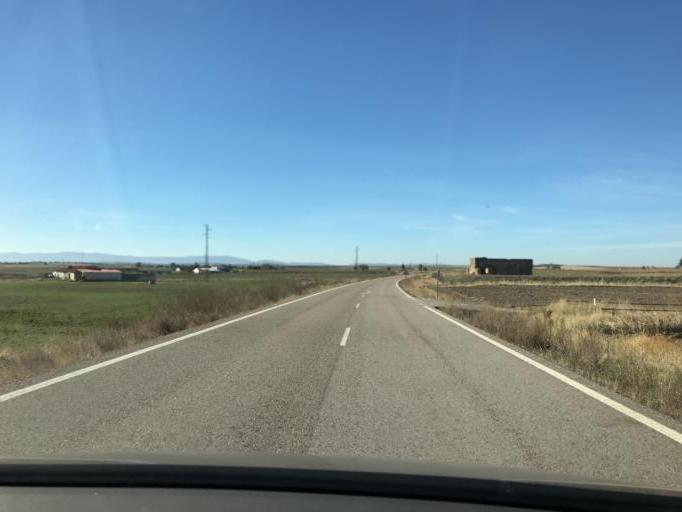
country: ES
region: Extremadura
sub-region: Provincia de Badajoz
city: Azuaga
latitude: 38.2543
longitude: -5.7336
